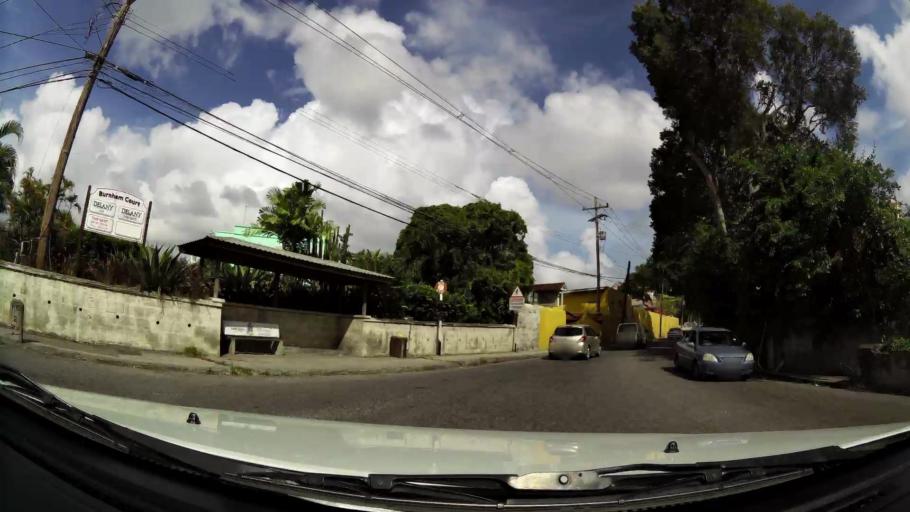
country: BB
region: Saint Michael
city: Bridgetown
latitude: 13.0940
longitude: -59.5996
